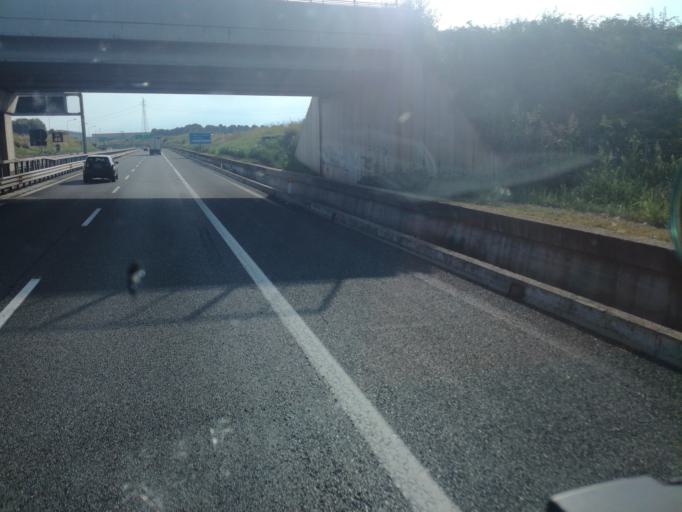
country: IT
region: Piedmont
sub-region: Provincia di Torino
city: Borgo Melano
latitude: 45.0081
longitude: 7.5719
